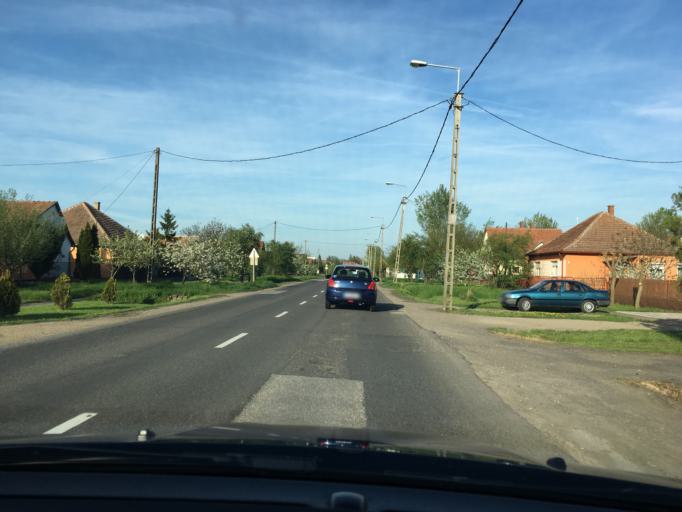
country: HU
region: Hajdu-Bihar
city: Csokmo
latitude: 47.0246
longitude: 21.2836
